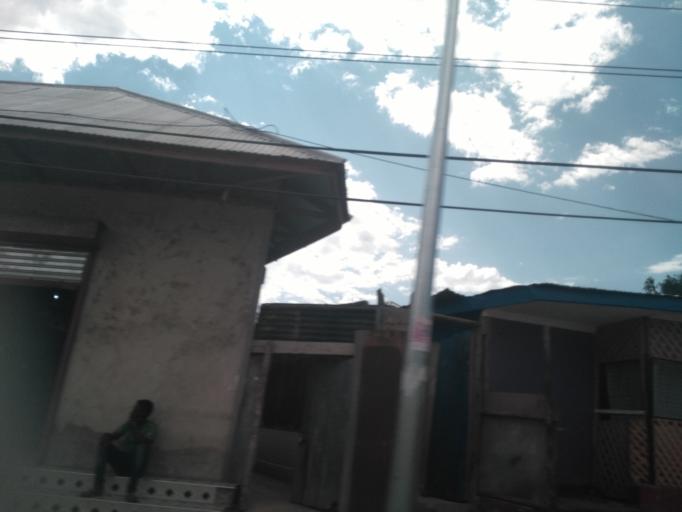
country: TZ
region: Mwanza
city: Mwanza
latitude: -2.5159
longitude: 32.9040
